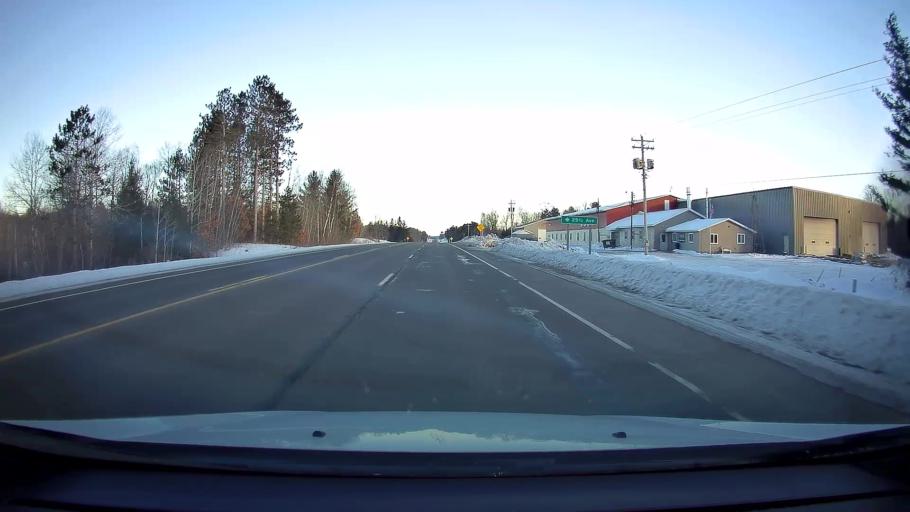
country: US
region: Wisconsin
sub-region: Barron County
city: Cumberland
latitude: 45.5719
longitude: -92.0174
